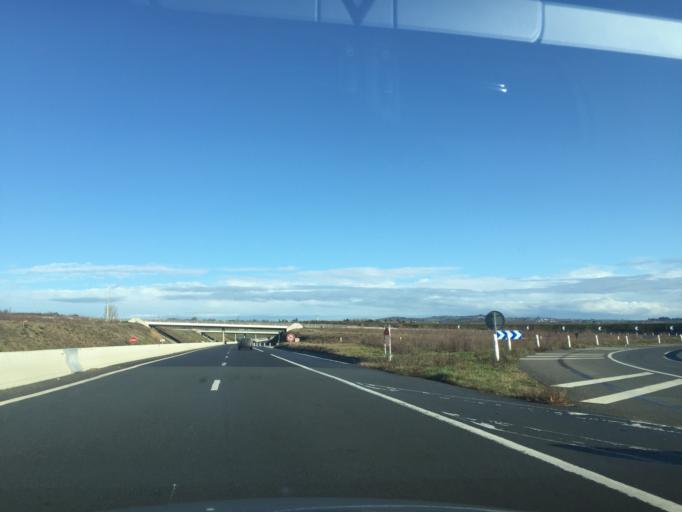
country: FR
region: Rhone-Alpes
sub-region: Departement de la Loire
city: Balbigny
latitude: 45.8360
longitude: 4.1635
